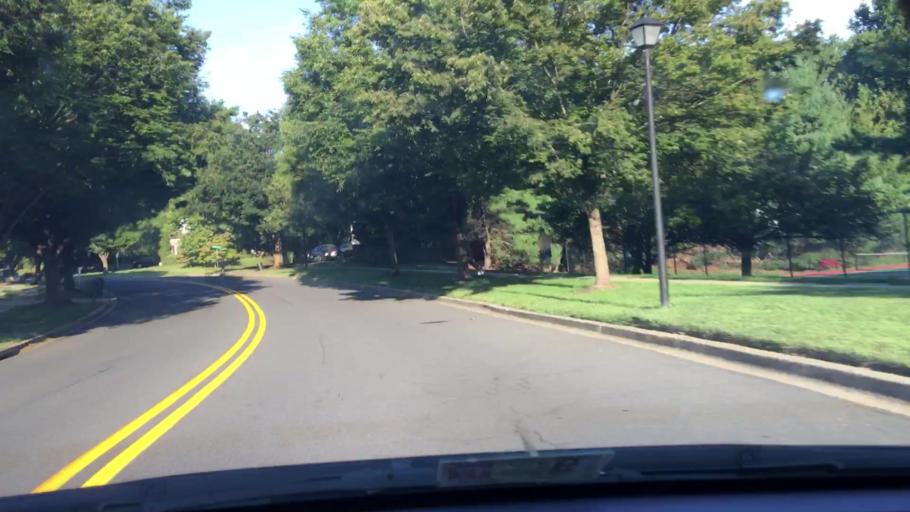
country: US
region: Maryland
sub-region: Montgomery County
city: Olney
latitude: 39.1572
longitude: -77.0557
